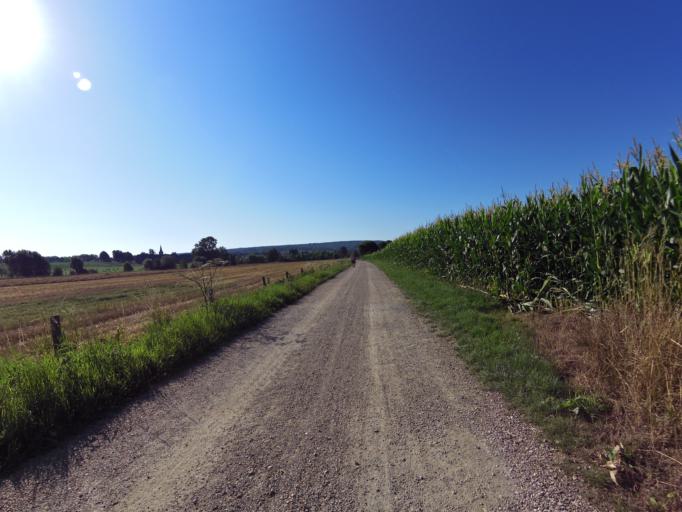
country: NL
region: Limburg
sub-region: Gemeente Voerendaal
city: Ubachsberg
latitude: 50.8001
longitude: 5.9160
